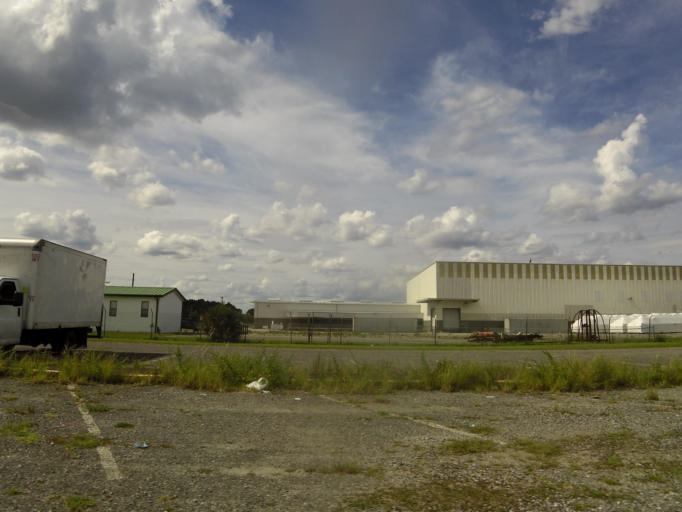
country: US
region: Florida
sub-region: Clay County
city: Green Cove Springs
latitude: 29.9773
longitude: -81.6588
